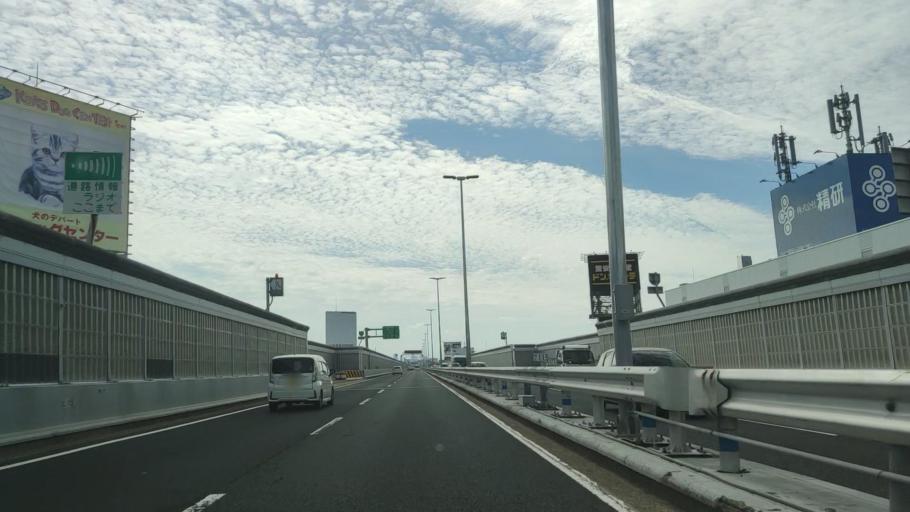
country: JP
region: Osaka
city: Toyonaka
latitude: 34.7759
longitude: 135.4578
